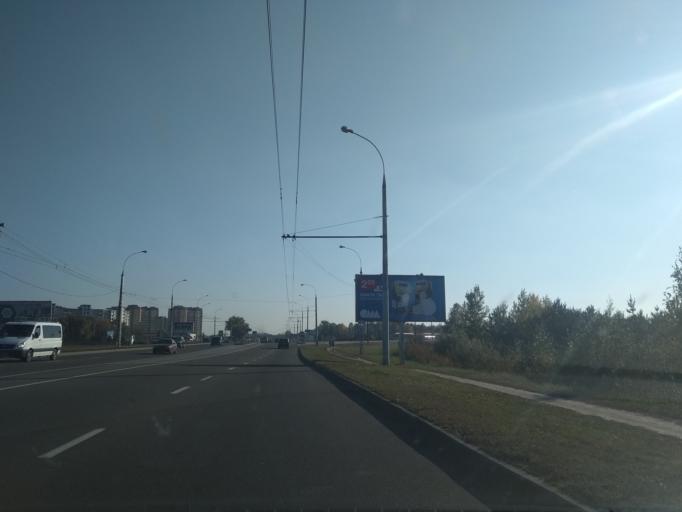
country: BY
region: Brest
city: Brest
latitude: 52.0828
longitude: 23.7368
